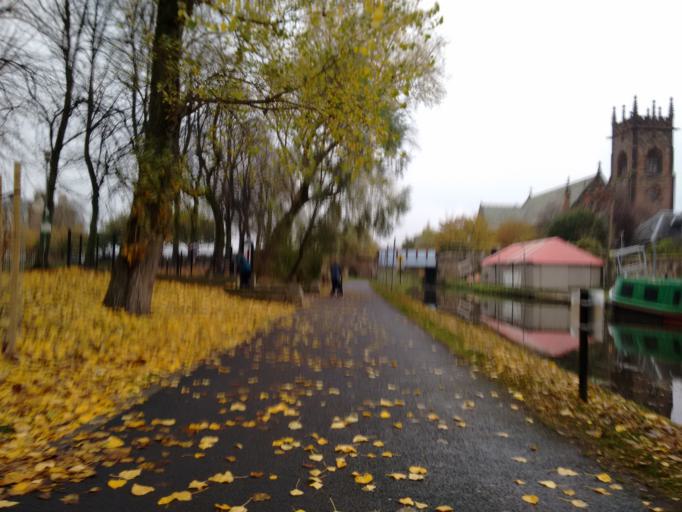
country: GB
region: Scotland
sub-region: Edinburgh
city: Edinburgh
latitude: 55.9333
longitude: -3.2252
